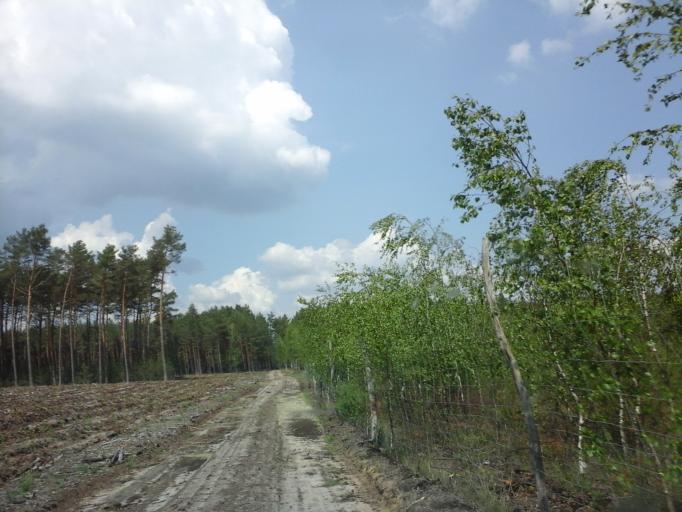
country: PL
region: West Pomeranian Voivodeship
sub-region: Powiat drawski
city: Kalisz Pomorski
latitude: 53.1779
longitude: 15.9319
